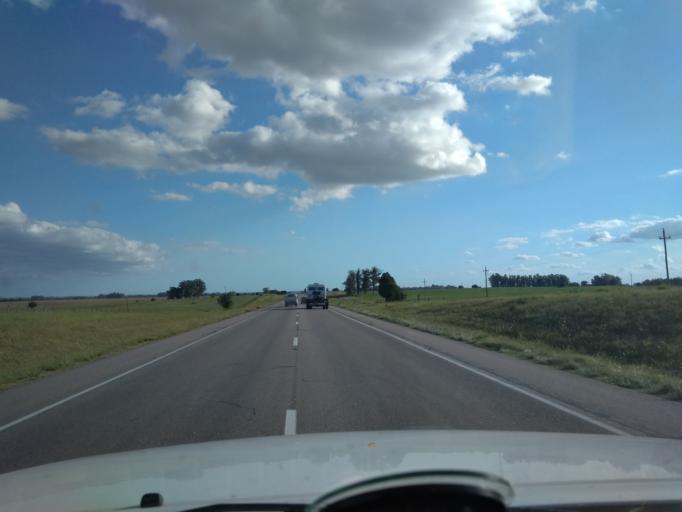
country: UY
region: Florida
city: Cardal
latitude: -34.3089
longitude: -56.2355
